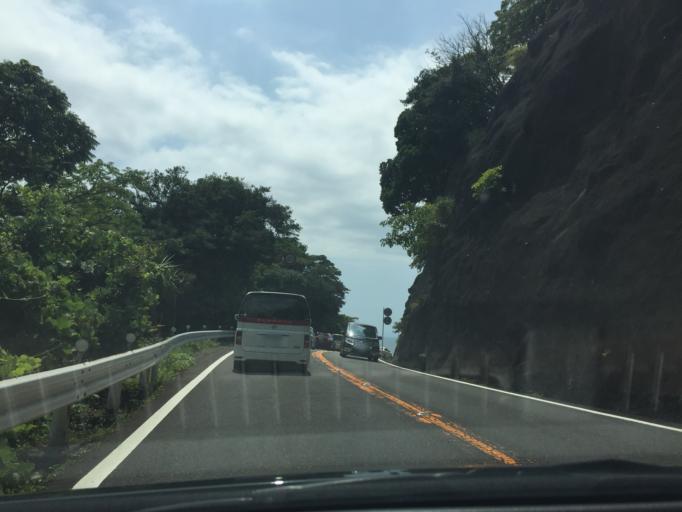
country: JP
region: Shizuoka
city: Shimoda
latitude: 34.7254
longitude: 138.9907
